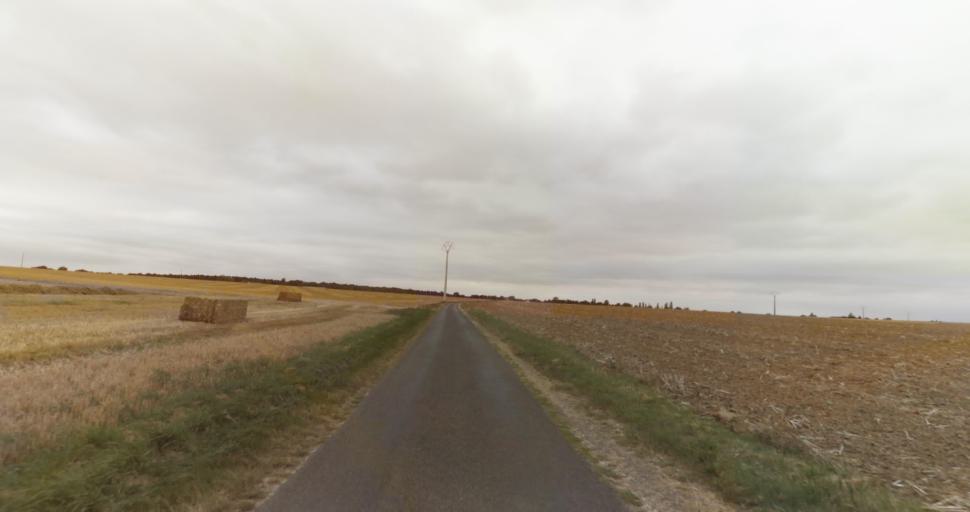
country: FR
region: Haute-Normandie
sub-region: Departement de l'Eure
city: La Couture-Boussey
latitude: 48.9092
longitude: 1.4038
